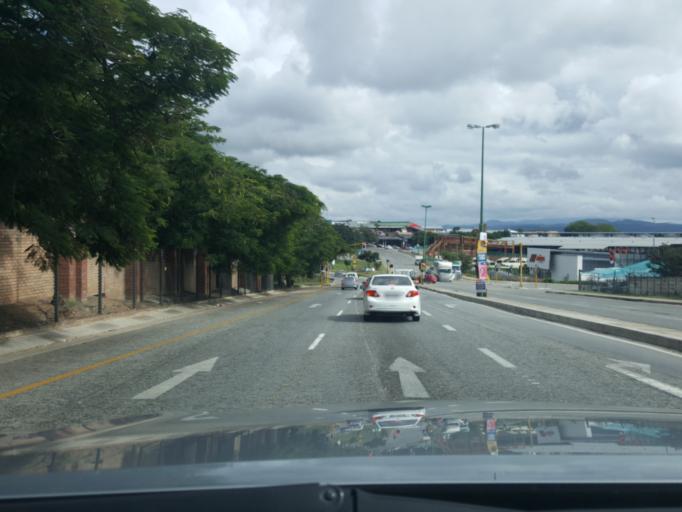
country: ZA
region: Mpumalanga
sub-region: Ehlanzeni District
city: Nelspruit
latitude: -25.4703
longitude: 30.9859
